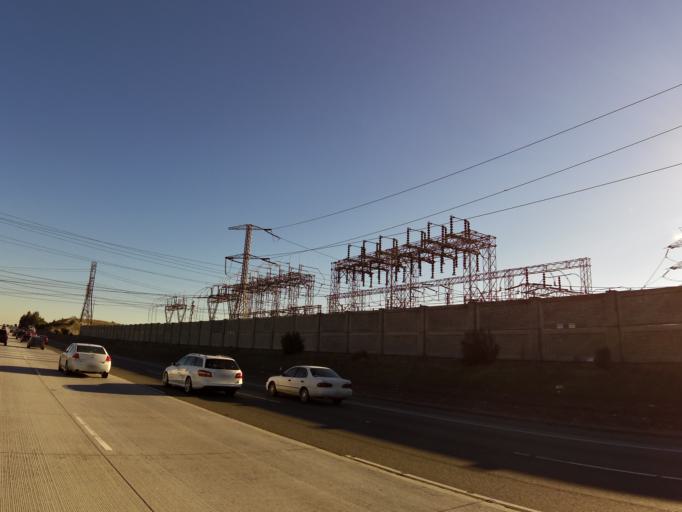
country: US
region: California
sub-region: Santa Clara County
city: Seven Trees
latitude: 37.2258
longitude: -121.7416
